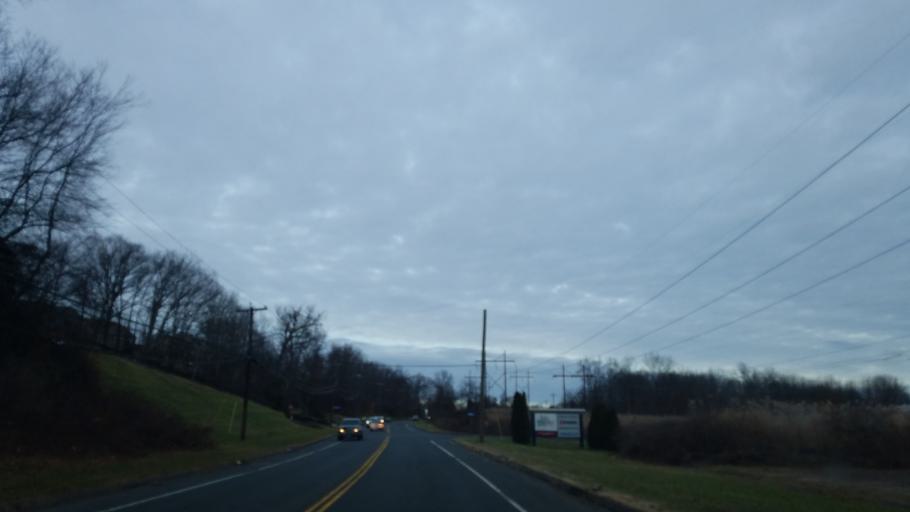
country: US
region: Connecticut
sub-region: Hartford County
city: Newington
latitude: 41.7060
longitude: -72.7504
